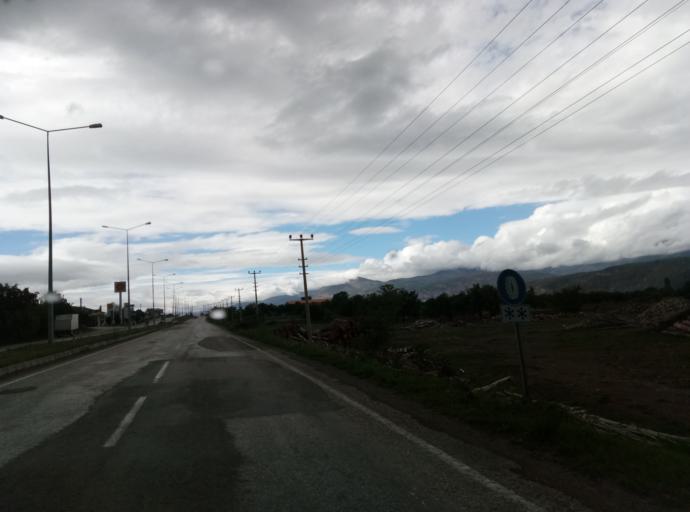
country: TR
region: Sivas
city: Susehri
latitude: 40.1723
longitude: 38.0894
